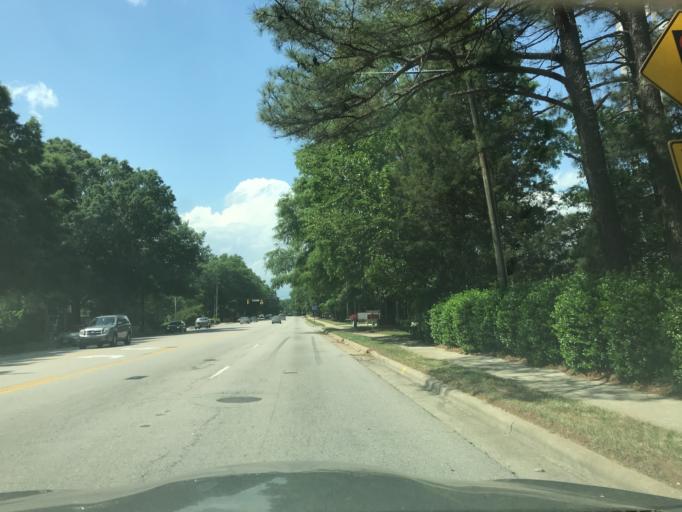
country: US
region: North Carolina
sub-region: Wake County
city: West Raleigh
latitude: 35.8702
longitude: -78.6404
